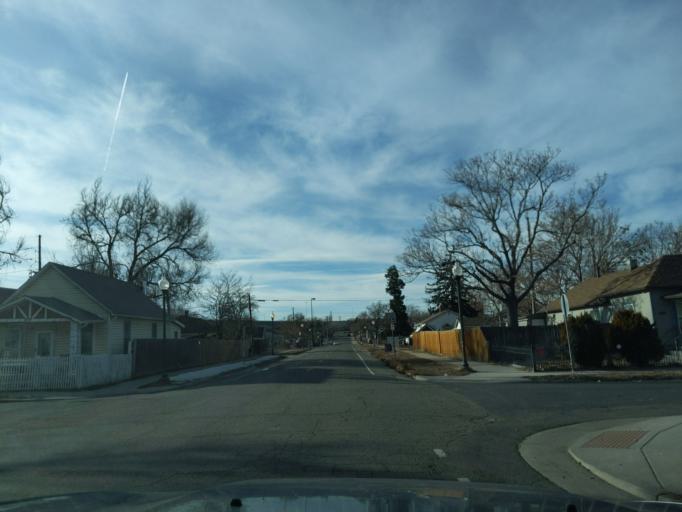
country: US
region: Colorado
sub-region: Denver County
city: Denver
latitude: 39.7820
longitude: -104.9833
